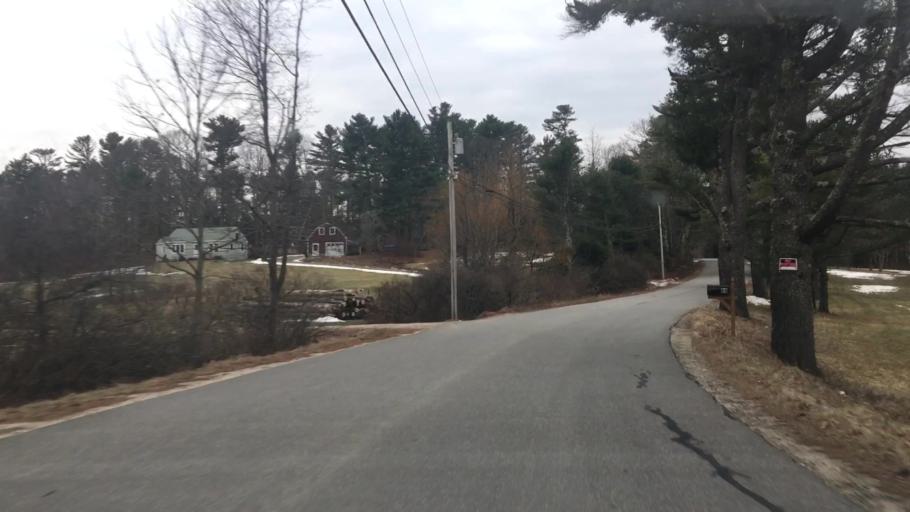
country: US
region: Maine
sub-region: Cumberland County
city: Freeport
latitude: 43.8464
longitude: -70.0666
